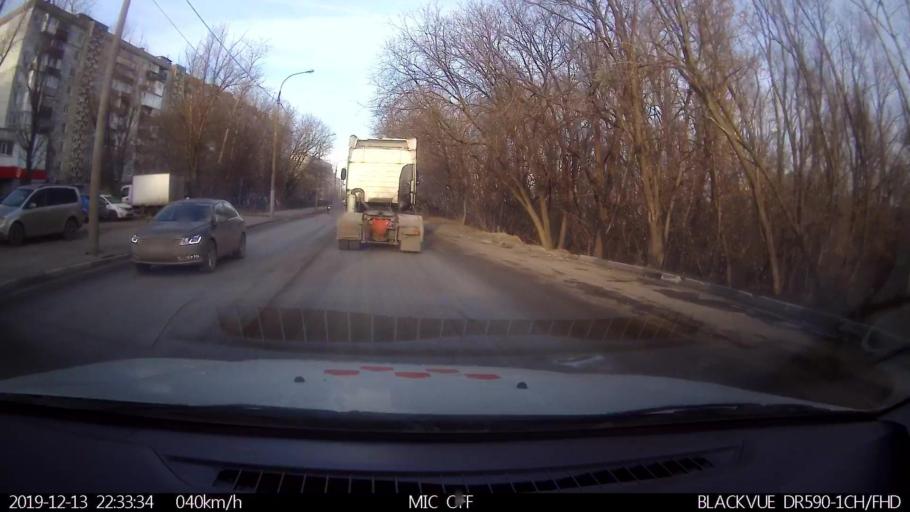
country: RU
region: Nizjnij Novgorod
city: Nizhniy Novgorod
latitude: 56.2886
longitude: 43.9531
